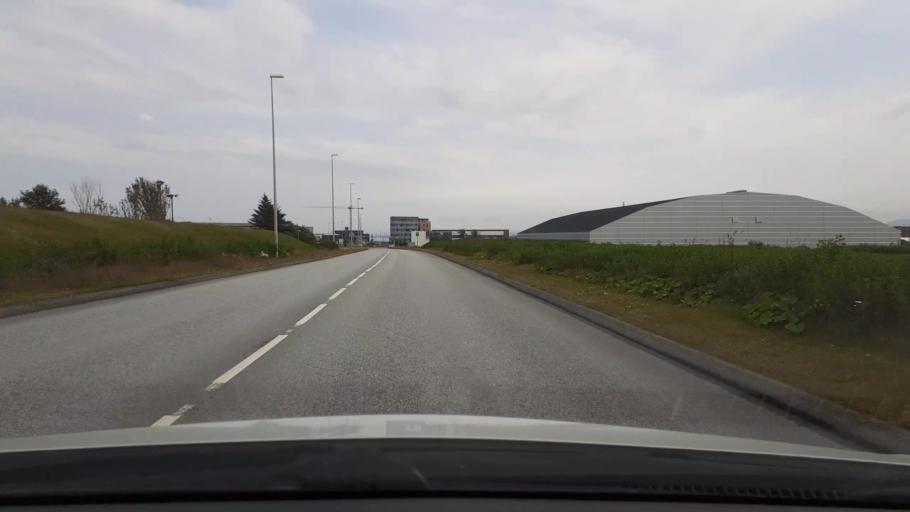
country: IS
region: Southern Peninsula
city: Reykjanesbaer
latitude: 63.9946
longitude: -22.5628
